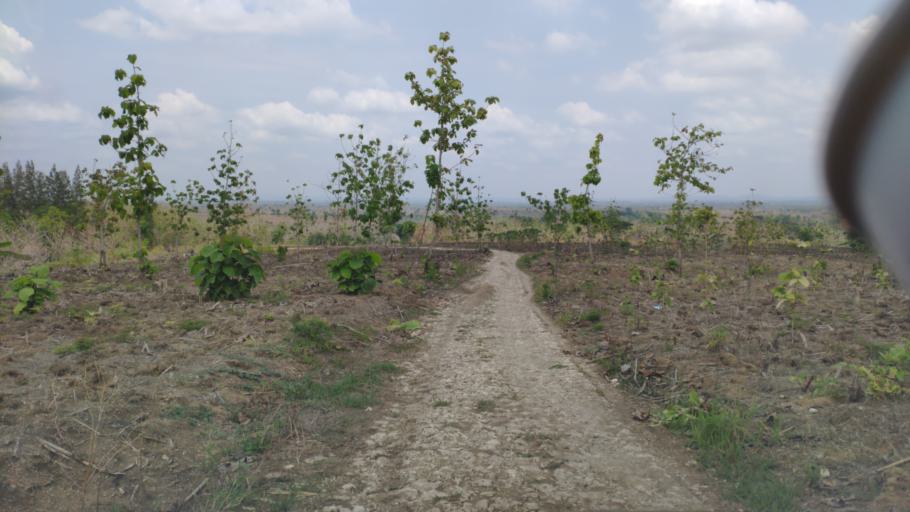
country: ID
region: Central Java
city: Gumiring
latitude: -7.0507
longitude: 111.3990
